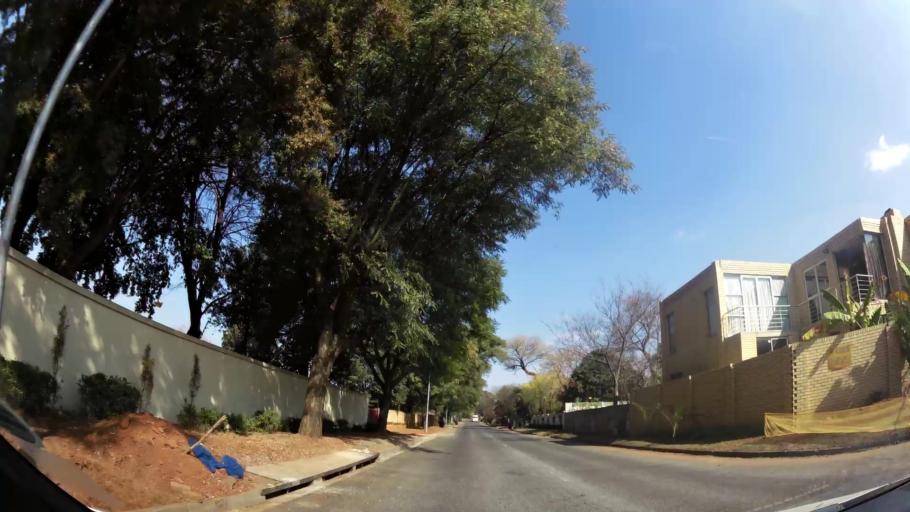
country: ZA
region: Gauteng
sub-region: Ekurhuleni Metropolitan Municipality
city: Benoni
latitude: -26.1885
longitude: 28.2896
